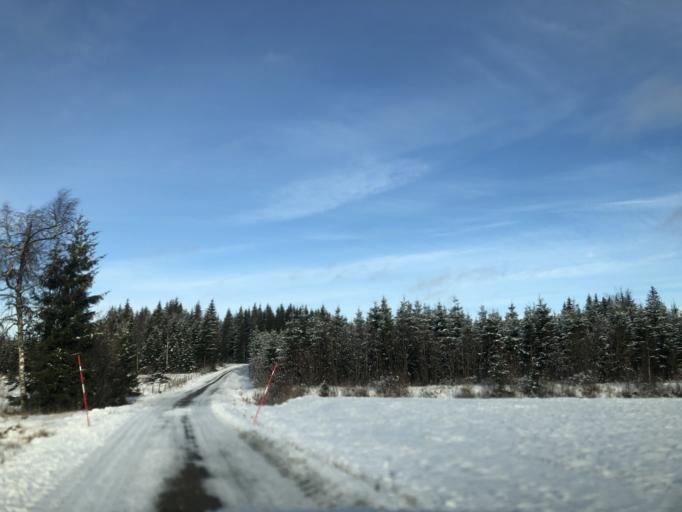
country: SE
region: Vaestra Goetaland
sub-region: Ulricehamns Kommun
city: Ulricehamn
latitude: 57.7382
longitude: 13.4930
